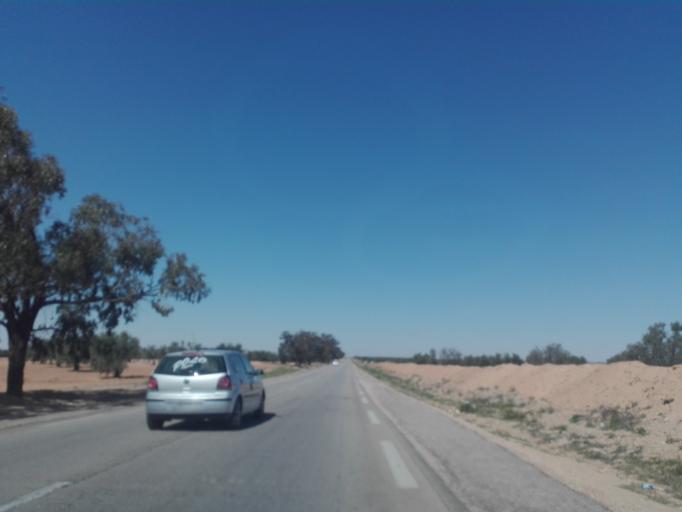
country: TN
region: Safaqis
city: Bi'r `Ali Bin Khalifah
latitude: 34.7574
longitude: 10.3189
